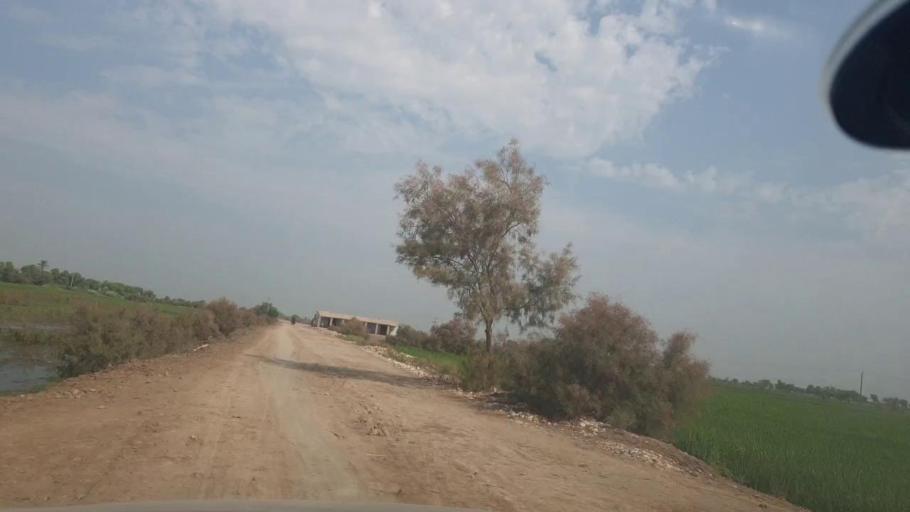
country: PK
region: Balochistan
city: Mehrabpur
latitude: 28.1040
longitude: 68.0919
